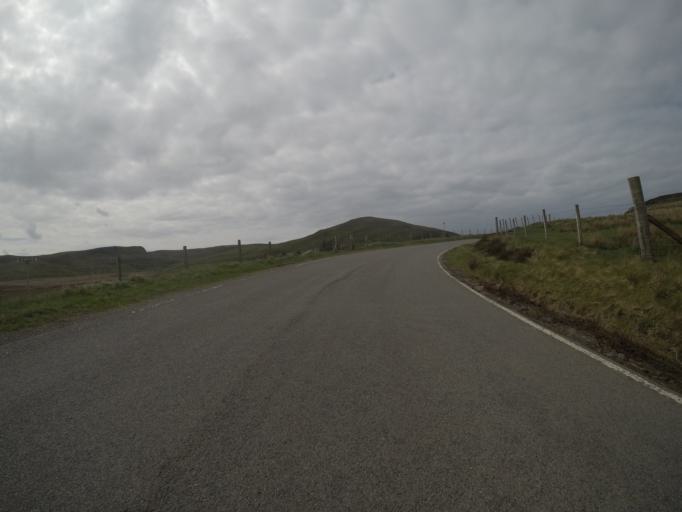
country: GB
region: Scotland
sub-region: Highland
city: Portree
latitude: 57.6822
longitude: -6.3226
